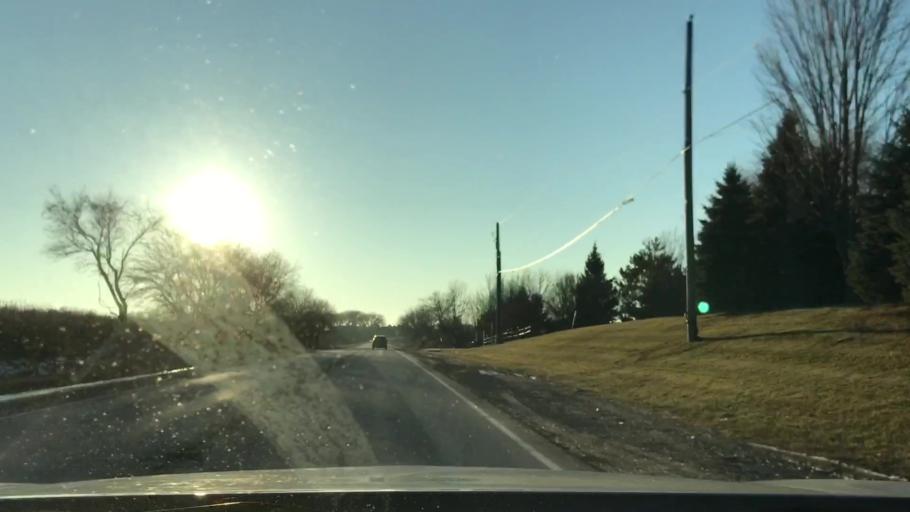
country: US
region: Illinois
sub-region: Kane County
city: Pingree Grove
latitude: 42.0914
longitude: -88.4203
